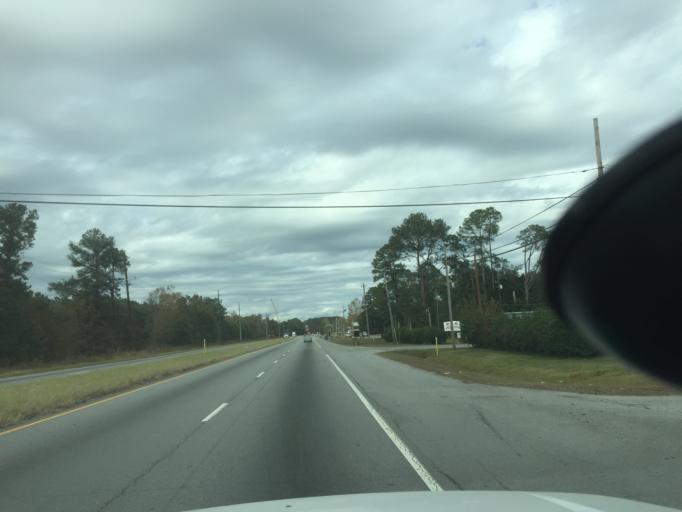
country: US
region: Georgia
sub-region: Chatham County
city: Port Wentworth
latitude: 32.1644
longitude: -81.1846
